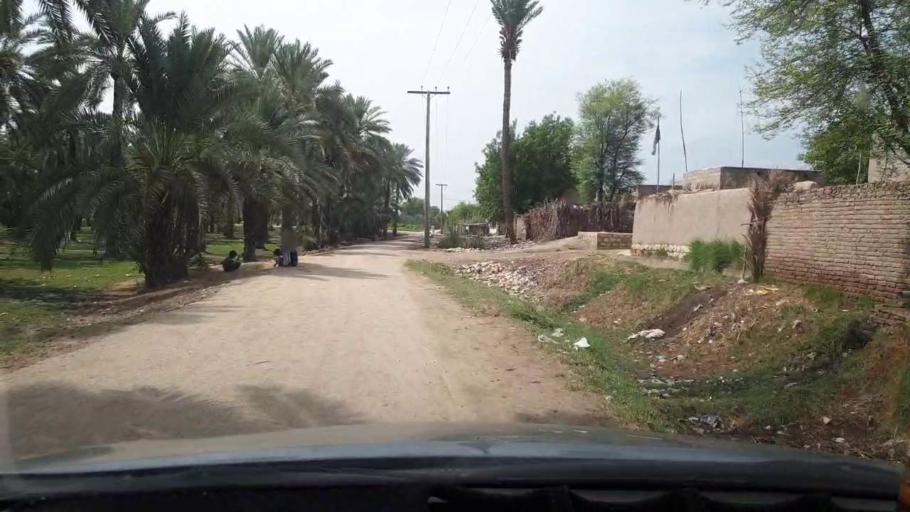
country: PK
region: Sindh
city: Khairpur
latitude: 27.4931
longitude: 68.7546
